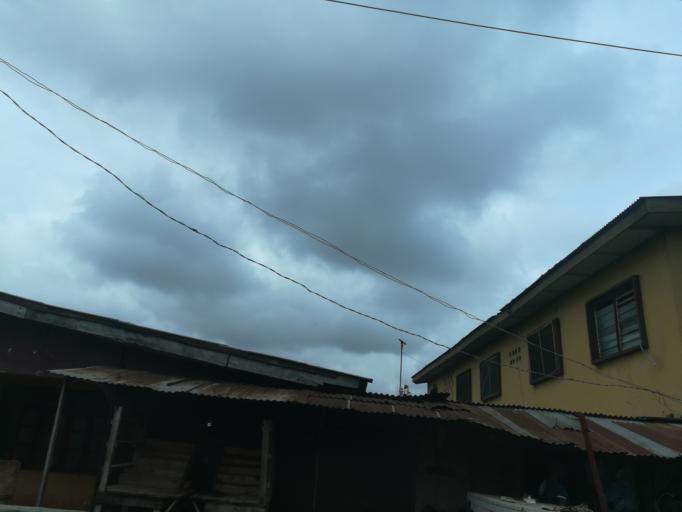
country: NG
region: Lagos
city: Oshodi
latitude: 6.5600
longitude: 3.3401
